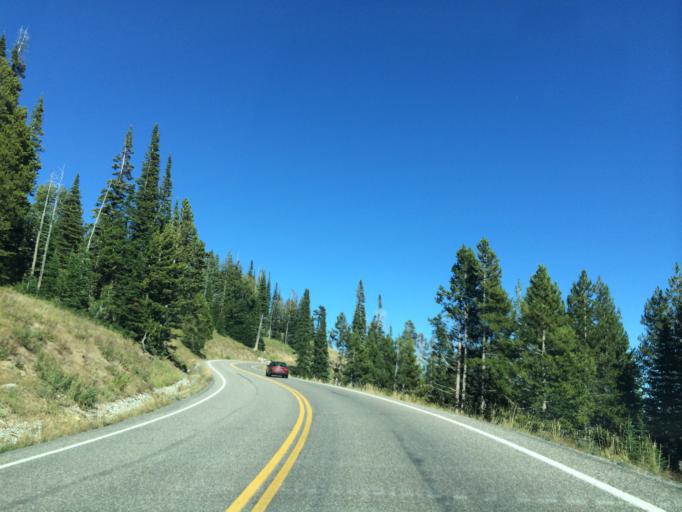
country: US
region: Montana
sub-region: Gallatin County
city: West Yellowstone
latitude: 44.7660
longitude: -110.4605
